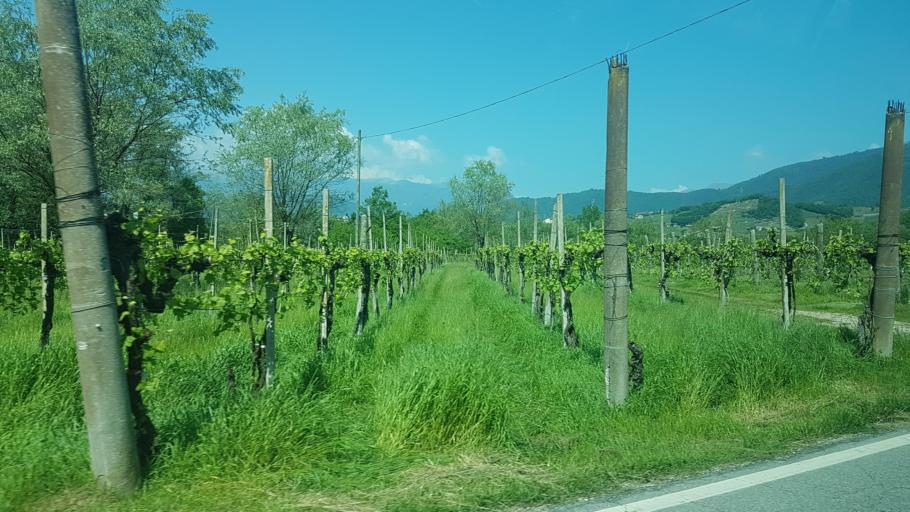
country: IT
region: Veneto
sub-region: Provincia di Treviso
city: Vidor
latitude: 45.8828
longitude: 12.0352
